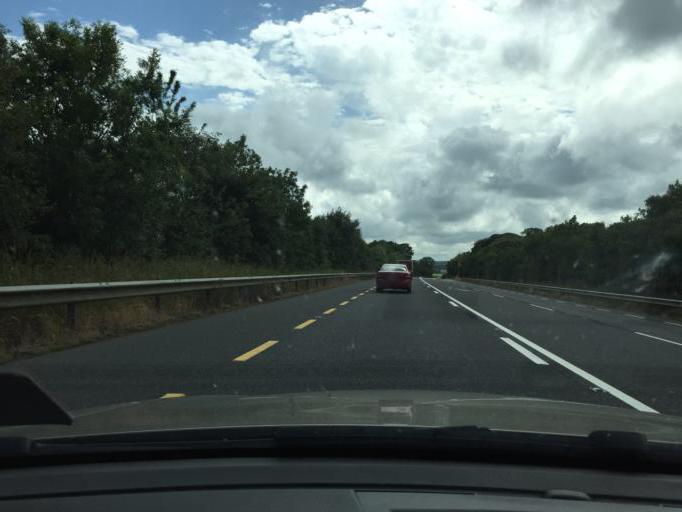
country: IE
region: Munster
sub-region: Waterford
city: Portlaw
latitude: 52.2079
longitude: -7.3991
